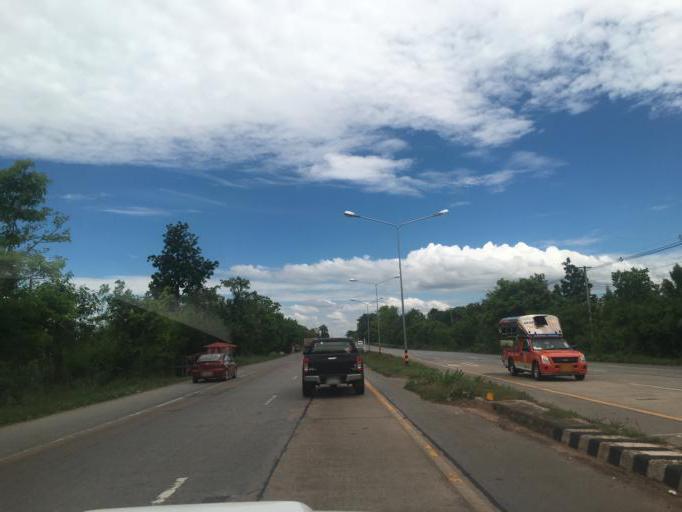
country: TH
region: Khon Kaen
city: Nam Phong
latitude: 16.6501
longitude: 102.8002
